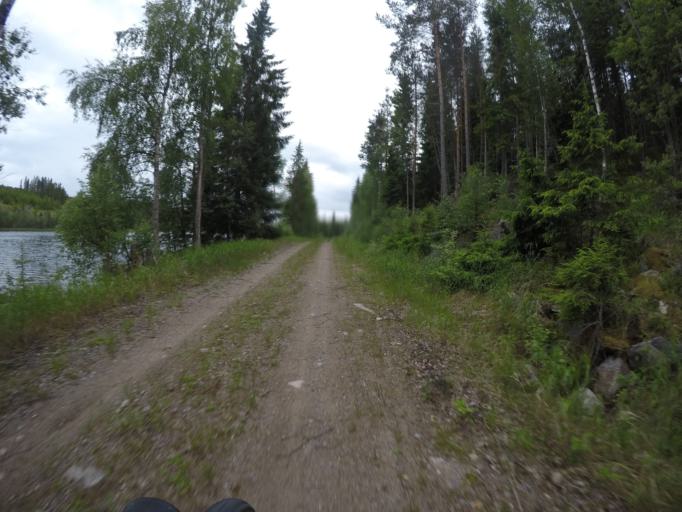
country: SE
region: Dalarna
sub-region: Ludvika Kommun
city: Abborrberget
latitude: 60.0463
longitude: 14.5911
